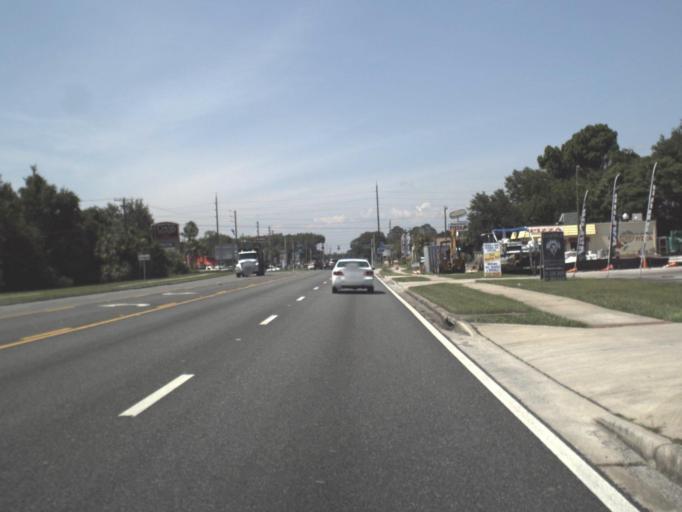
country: US
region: Florida
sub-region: Citrus County
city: Homosassa Springs
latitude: 28.8010
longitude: -82.5763
